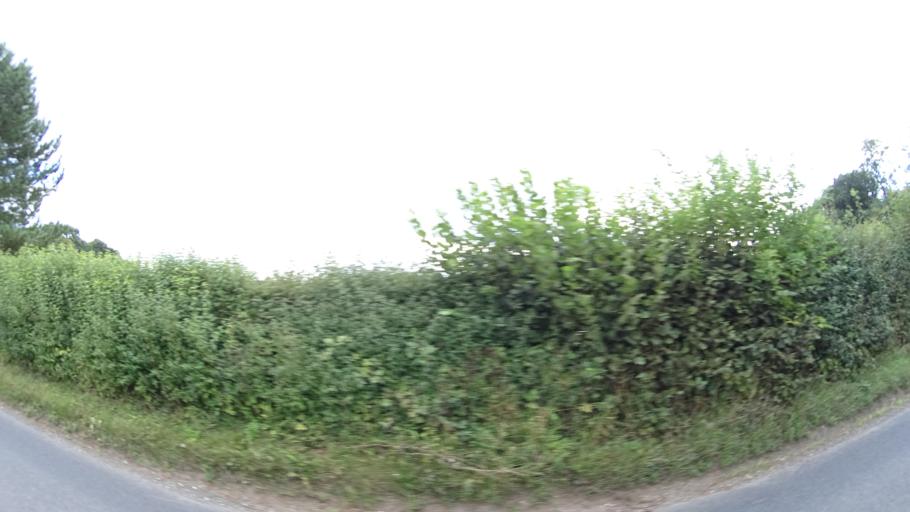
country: GB
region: England
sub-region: Hampshire
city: East Dean
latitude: 51.0669
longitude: -1.5511
